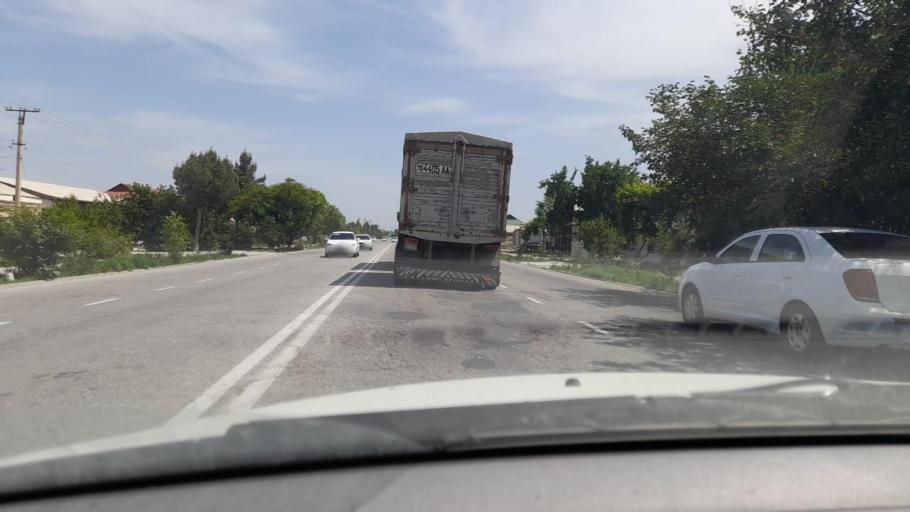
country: UZ
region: Navoiy
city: Karmana Shahri
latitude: 40.1418
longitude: 65.3896
